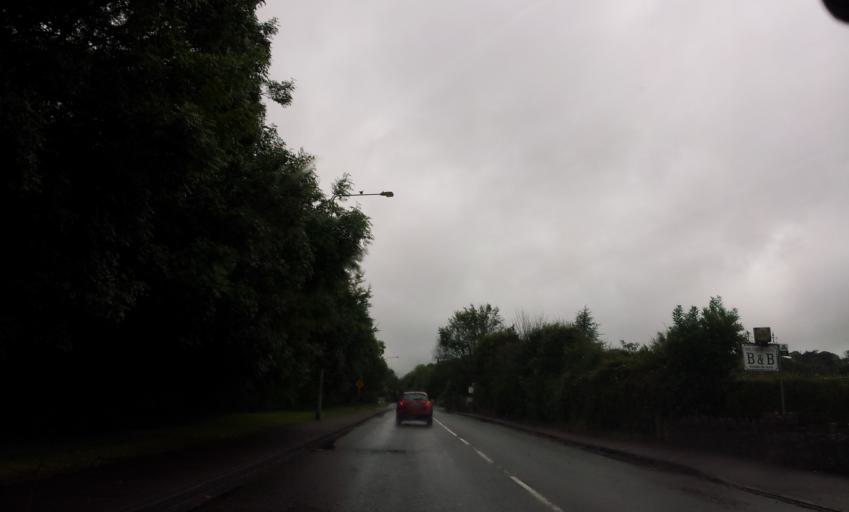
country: IE
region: Munster
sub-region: County Cork
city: Tower
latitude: 51.9299
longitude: -8.5903
